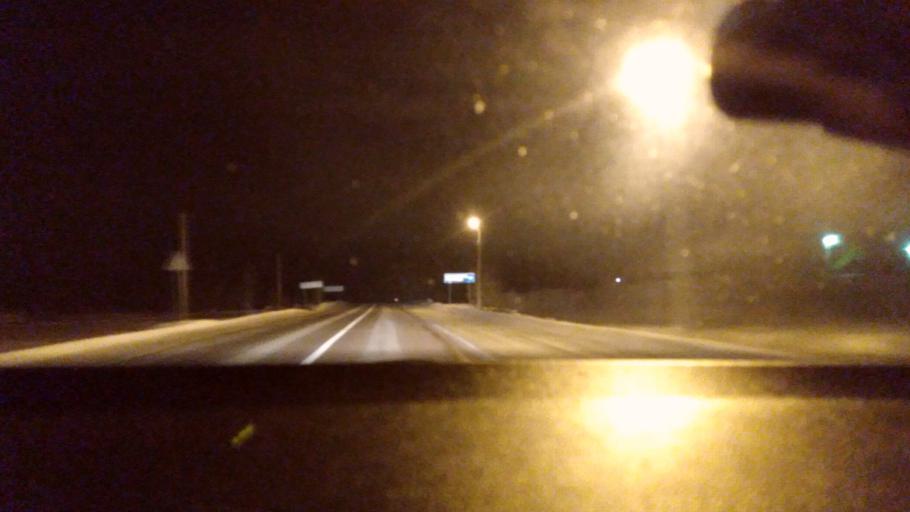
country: RU
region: Moskovskaya
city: Krasnaya Poyma
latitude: 55.1683
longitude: 39.1500
